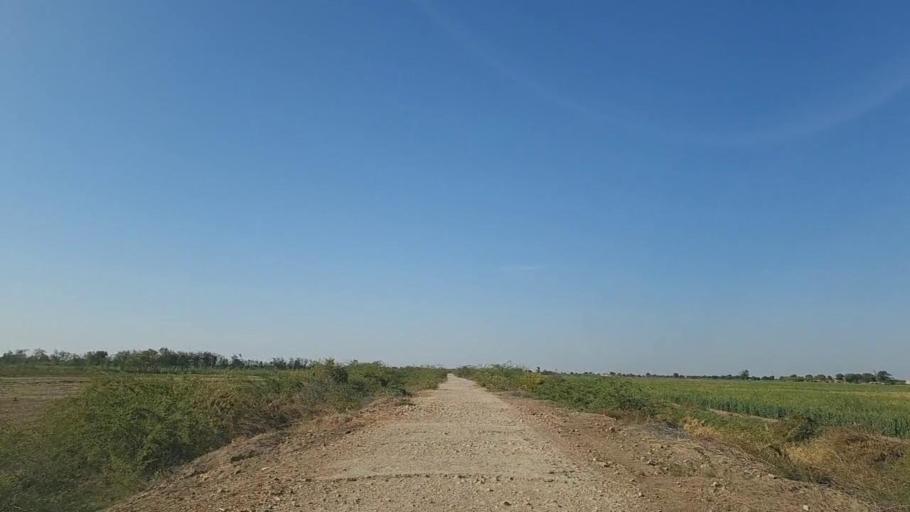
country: PK
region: Sindh
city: Kunri
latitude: 25.2463
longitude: 69.4960
